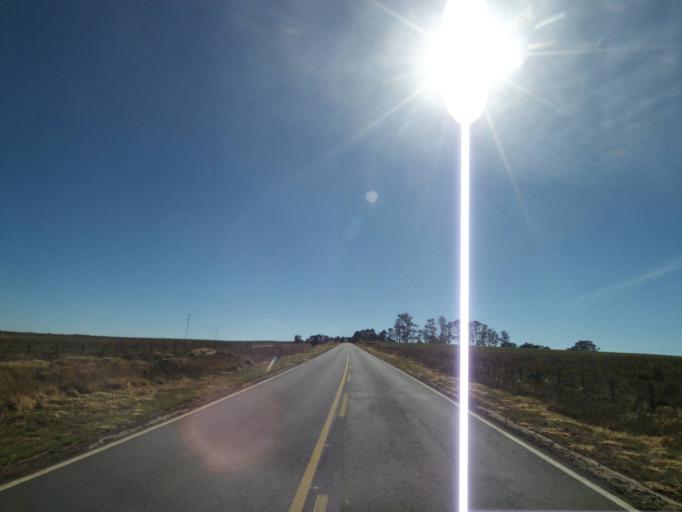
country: BR
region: Parana
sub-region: Castro
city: Castro
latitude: -24.6775
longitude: -50.2131
